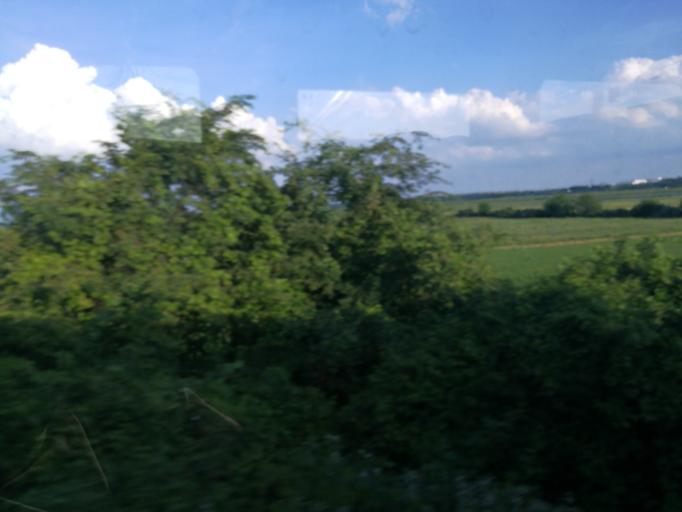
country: RO
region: Arges
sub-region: Oras Stefanesti
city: Golesti
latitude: 44.8361
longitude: 24.9427
